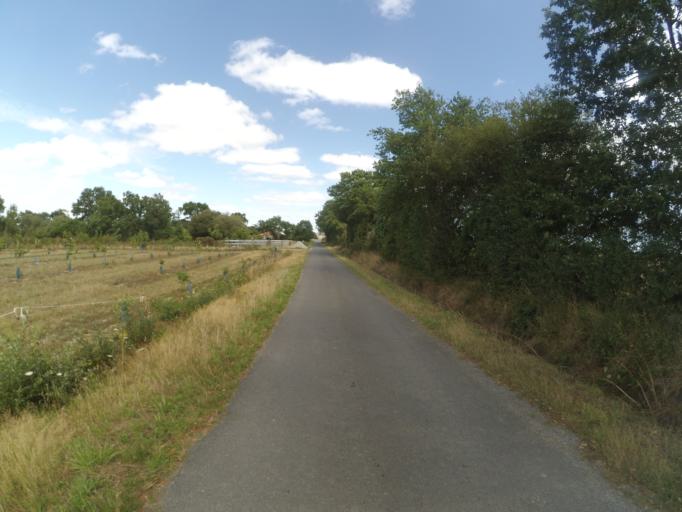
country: FR
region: Pays de la Loire
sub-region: Departement de la Loire-Atlantique
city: Remouille
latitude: 47.0456
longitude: -1.4029
